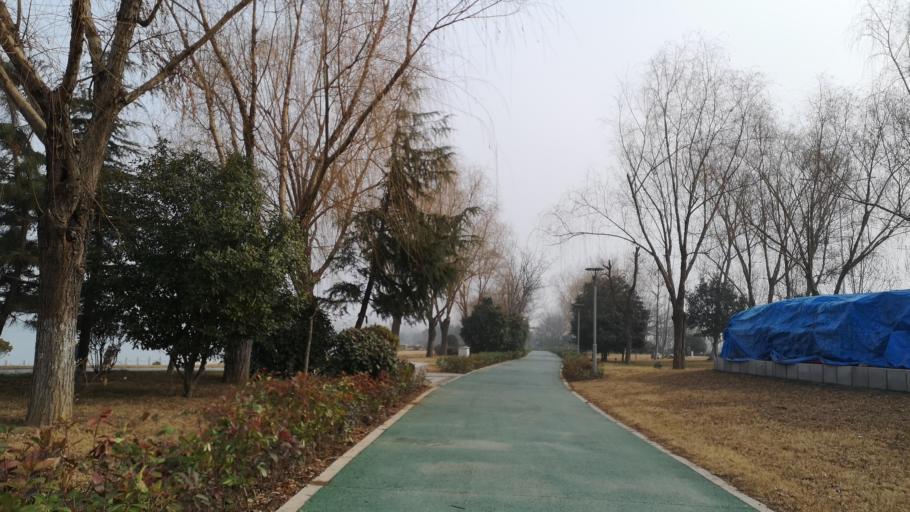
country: CN
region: Henan Sheng
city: Zhongyuanlu
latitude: 35.8003
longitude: 115.0525
